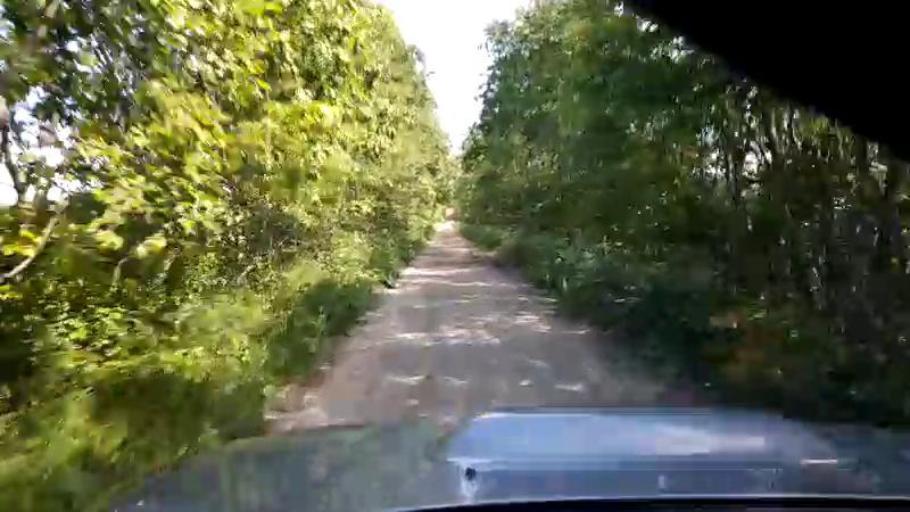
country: EE
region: Paernumaa
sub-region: Halinga vald
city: Parnu-Jaagupi
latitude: 58.5247
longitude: 24.5113
